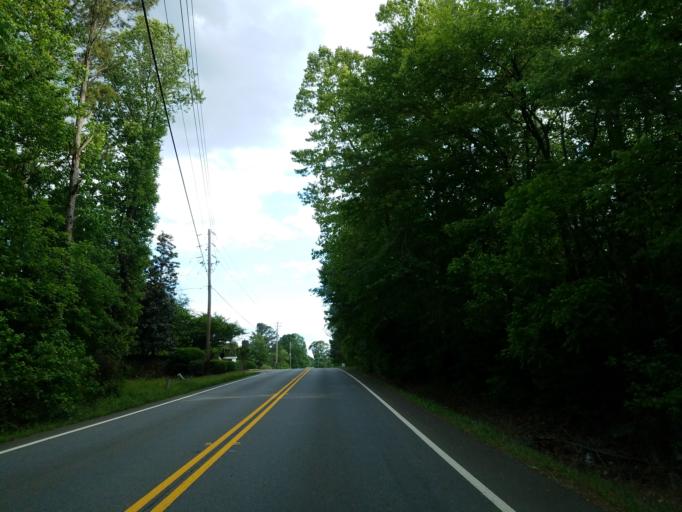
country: US
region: Georgia
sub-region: Cherokee County
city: Ball Ground
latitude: 34.2623
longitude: -84.2883
